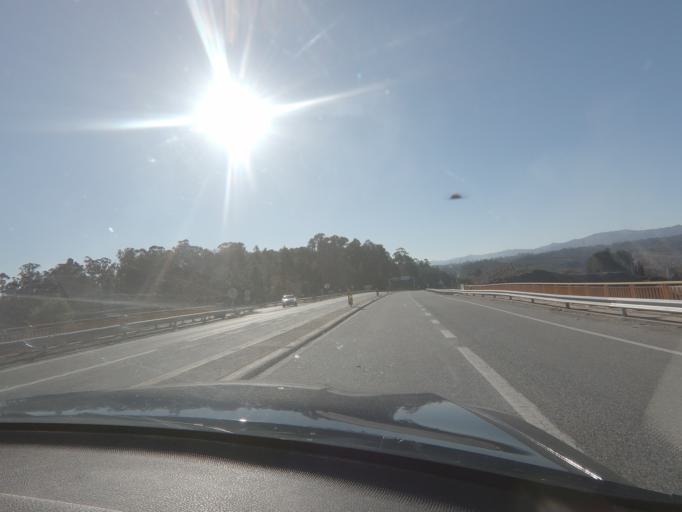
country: PT
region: Viseu
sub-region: Viseu
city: Abraveses
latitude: 40.6689
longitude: -7.9903
